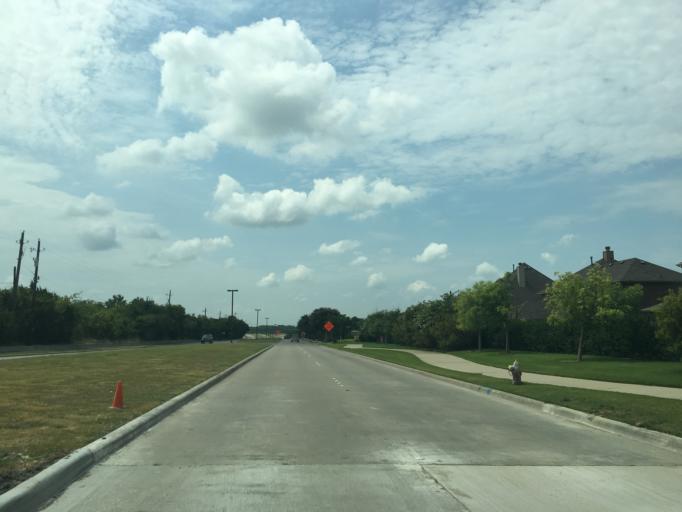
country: US
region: Texas
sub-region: Rockwall County
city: Rockwall
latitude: 32.9466
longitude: -96.4424
